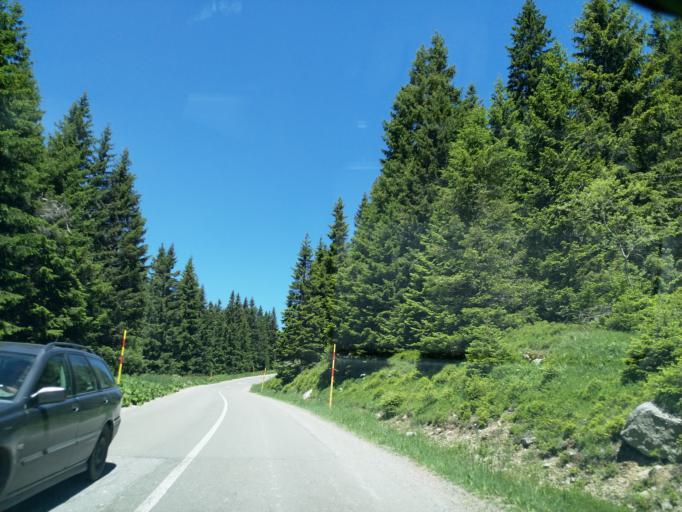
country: XK
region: Mitrovica
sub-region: Komuna e Leposaviqit
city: Leposaviq
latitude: 43.2958
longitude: 20.8186
